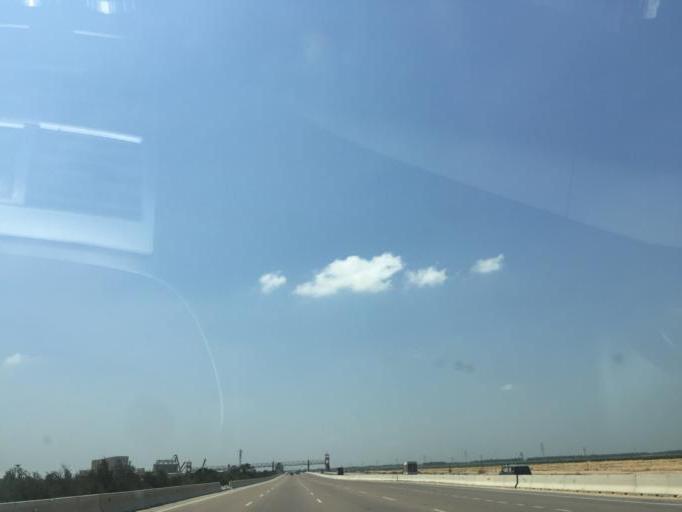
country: EG
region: Al Buhayrah
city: Abu al Matamir
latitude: 30.7096
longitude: 30.0396
